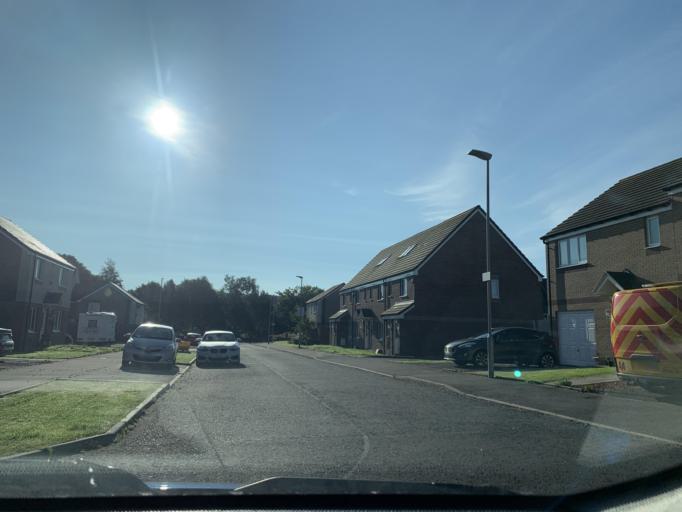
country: GB
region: Scotland
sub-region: East Renfrewshire
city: Giffnock
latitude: 55.8199
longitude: -4.3327
